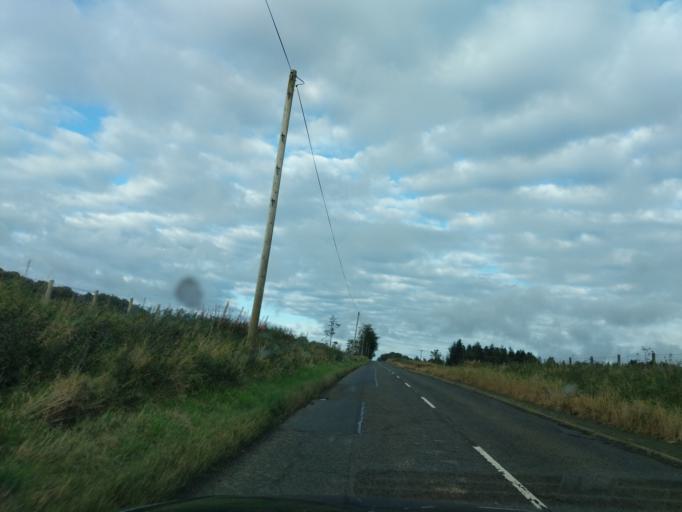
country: GB
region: Scotland
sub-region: Midlothian
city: Penicuik
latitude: 55.8203
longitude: -3.2708
